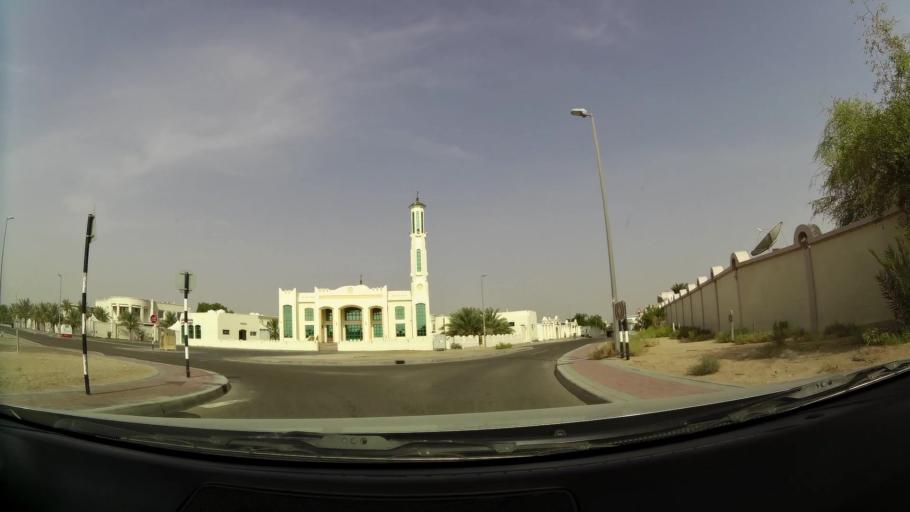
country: AE
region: Abu Dhabi
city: Al Ain
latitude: 24.1336
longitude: 55.7064
